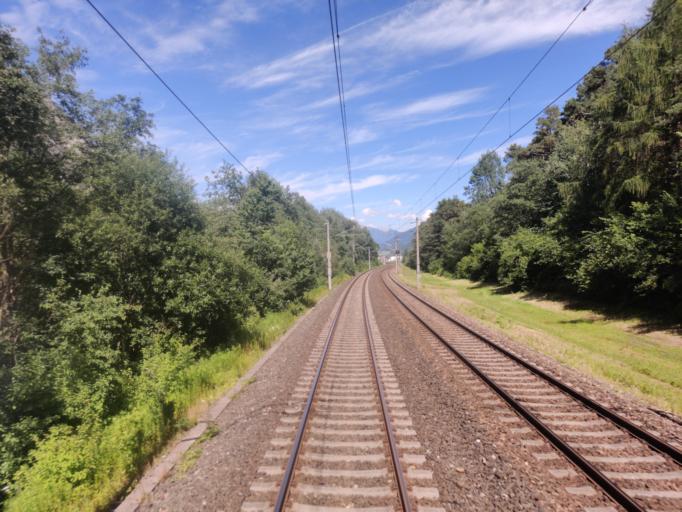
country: AT
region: Tyrol
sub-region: Politischer Bezirk Imst
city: Silz
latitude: 47.2656
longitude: 10.9102
